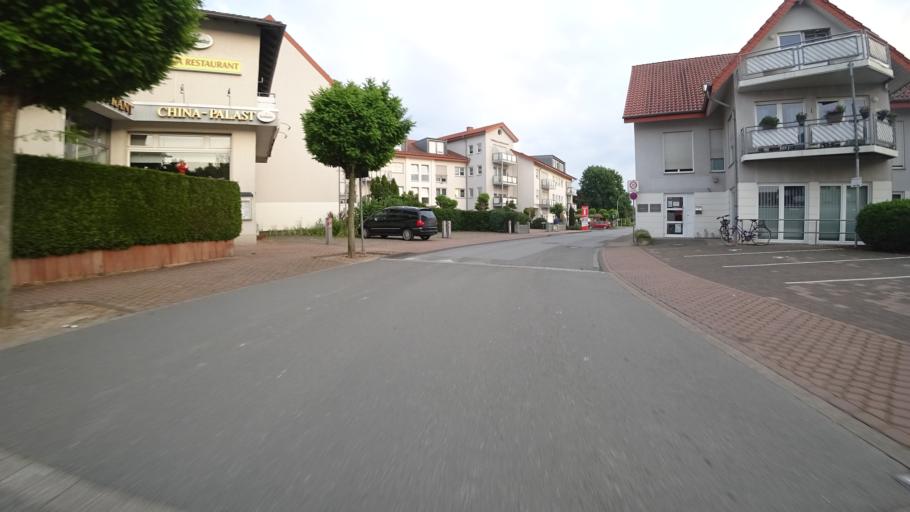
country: DE
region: North Rhine-Westphalia
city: Erwitte
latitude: 51.6313
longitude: 8.3605
